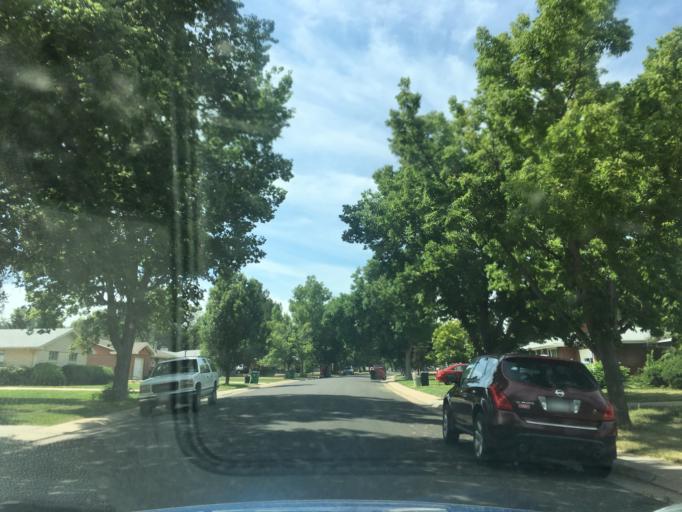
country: US
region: Colorado
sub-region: Adams County
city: Aurora
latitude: 39.7216
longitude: -104.8597
